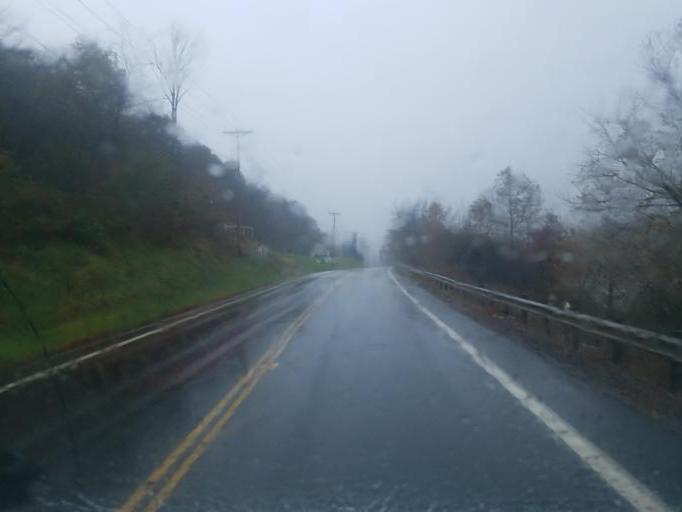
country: US
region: Ohio
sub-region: Morgan County
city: McConnelsville
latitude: 39.6652
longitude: -81.8673
